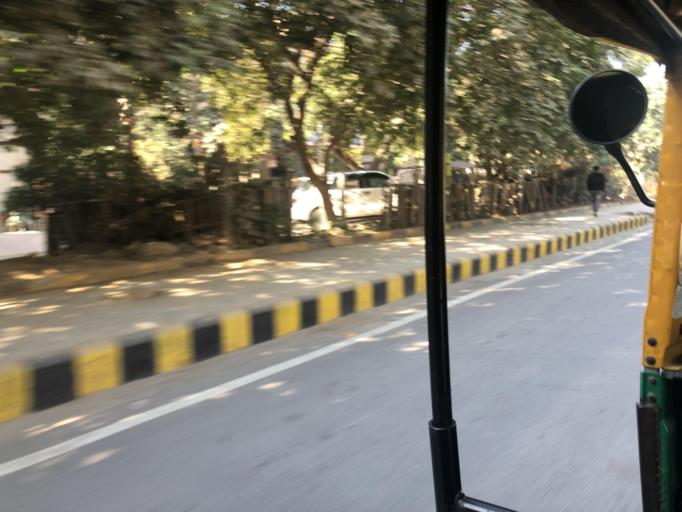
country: IN
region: Haryana
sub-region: Gurgaon
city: Gurgaon
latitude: 28.4509
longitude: 77.0685
